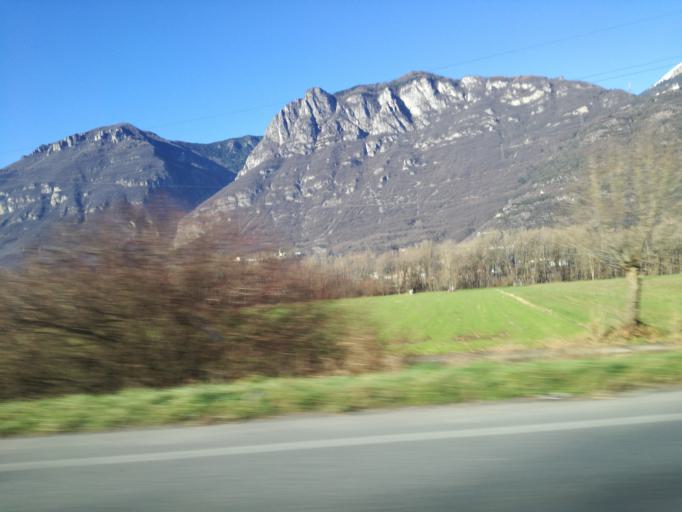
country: IT
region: Lombardy
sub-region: Provincia di Brescia
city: Pian Camuno
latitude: 45.8420
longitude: 10.1331
